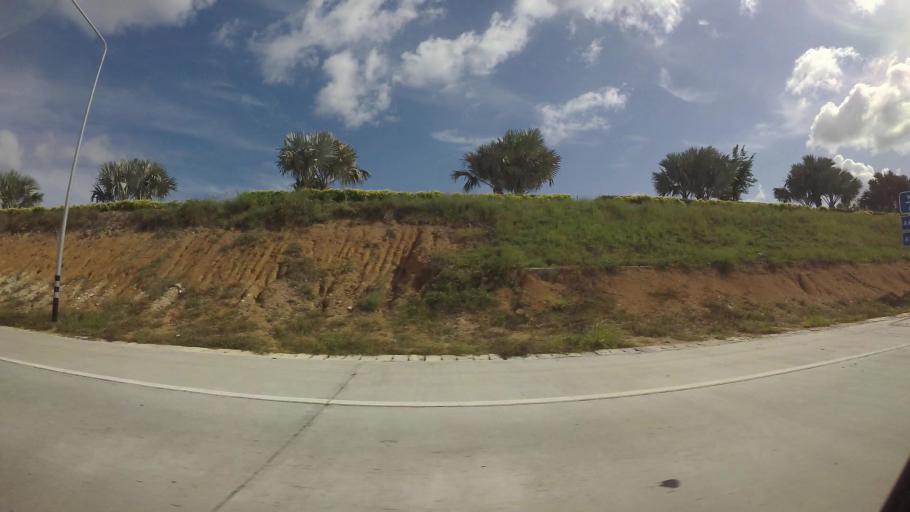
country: TH
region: Chon Buri
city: Phatthaya
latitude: 12.9519
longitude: 100.9641
